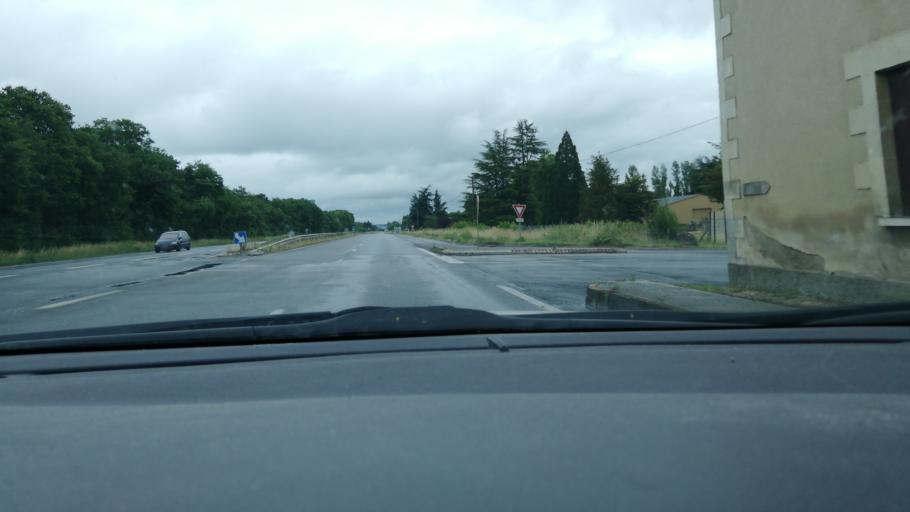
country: FR
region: Poitou-Charentes
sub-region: Departement de la Vienne
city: Naintre
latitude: 46.7682
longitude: 0.5026
